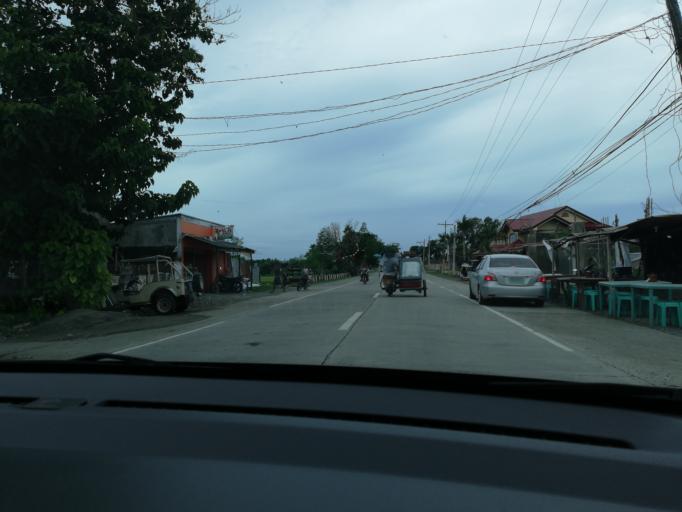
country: PH
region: Ilocos
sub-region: Province of Ilocos Sur
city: Bantay
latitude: 17.5830
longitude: 120.3782
